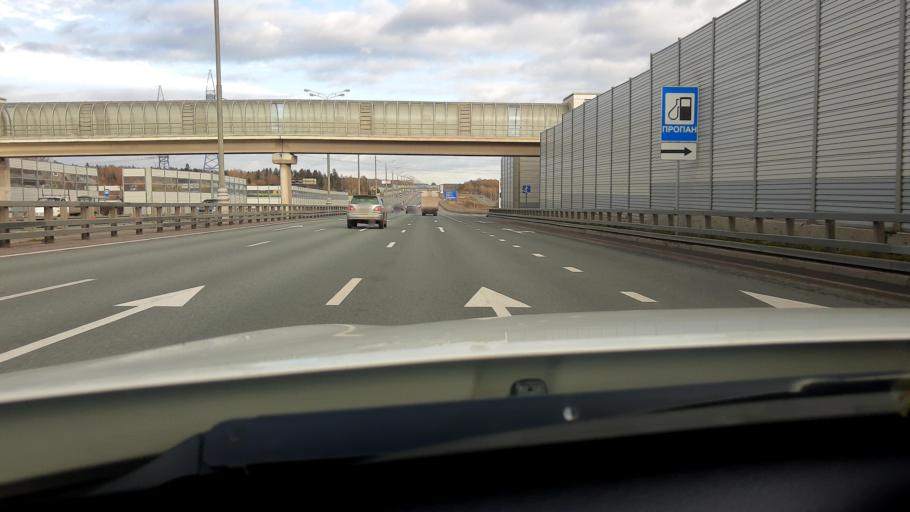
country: RU
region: Moskovskaya
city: Selyatino
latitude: 55.5229
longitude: 37.0146
